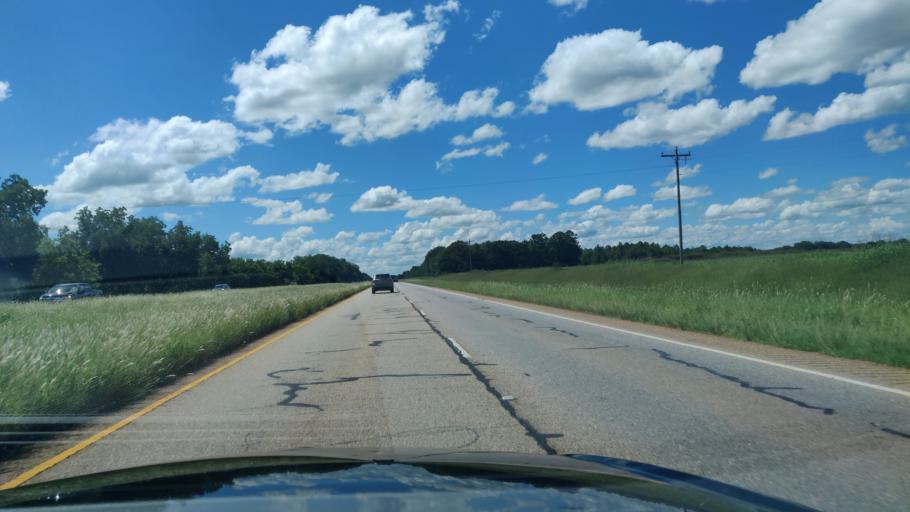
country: US
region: Georgia
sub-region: Webster County
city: Preston
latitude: 31.9557
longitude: -84.5867
